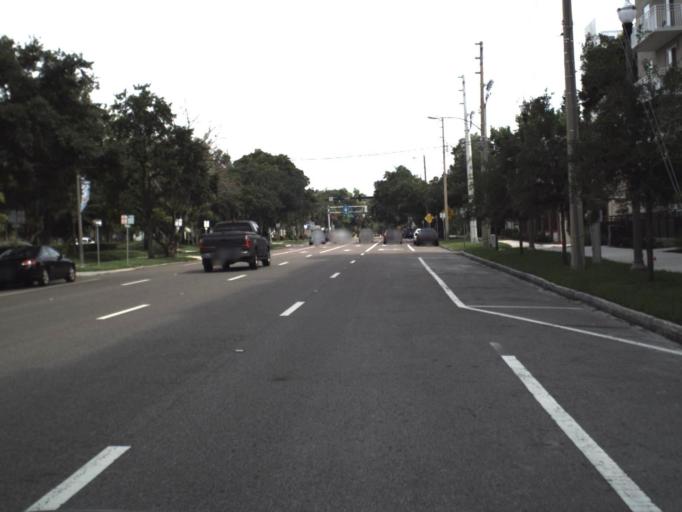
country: US
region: Florida
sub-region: Pinellas County
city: Saint Petersburg
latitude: 27.7751
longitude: -82.6371
